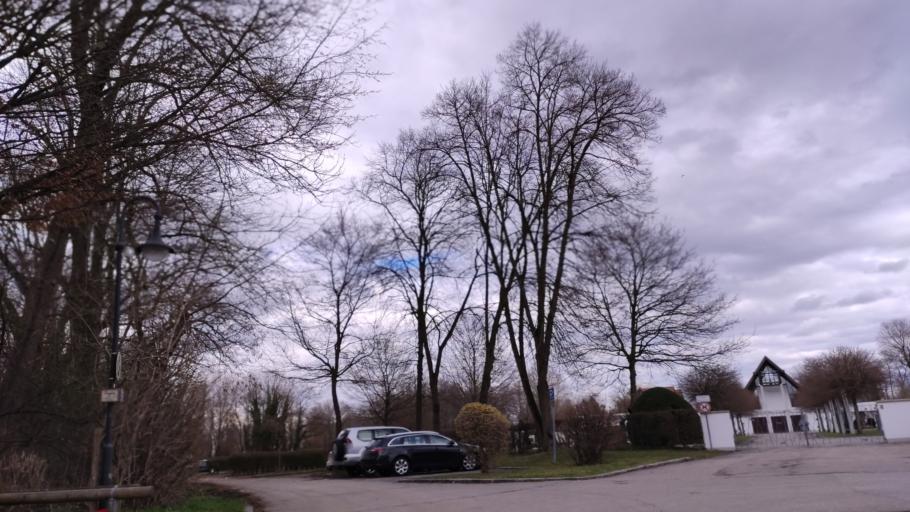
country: DE
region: Bavaria
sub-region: Upper Bavaria
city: Emmering
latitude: 48.1819
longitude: 11.2818
